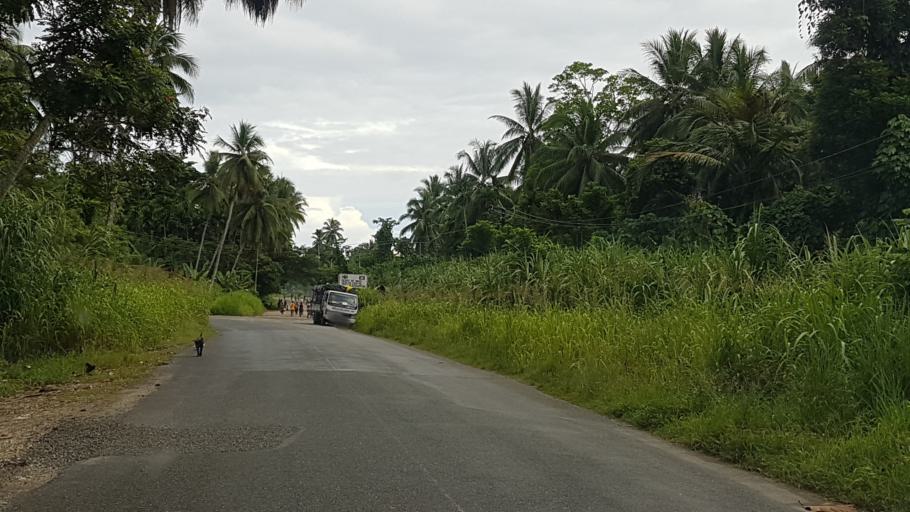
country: PG
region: Madang
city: Madang
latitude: -5.0983
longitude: 145.7947
